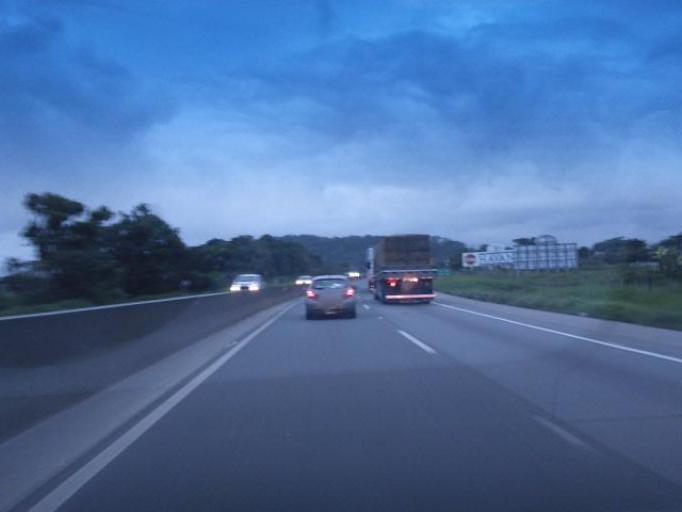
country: BR
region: Santa Catarina
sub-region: Barra Velha
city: Barra Velha
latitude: -26.5449
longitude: -48.7122
